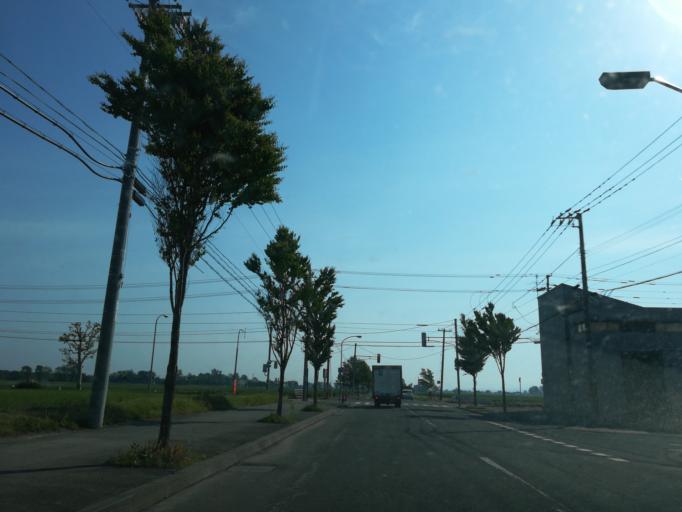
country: JP
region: Hokkaido
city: Iwamizawa
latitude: 43.1500
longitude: 141.6651
